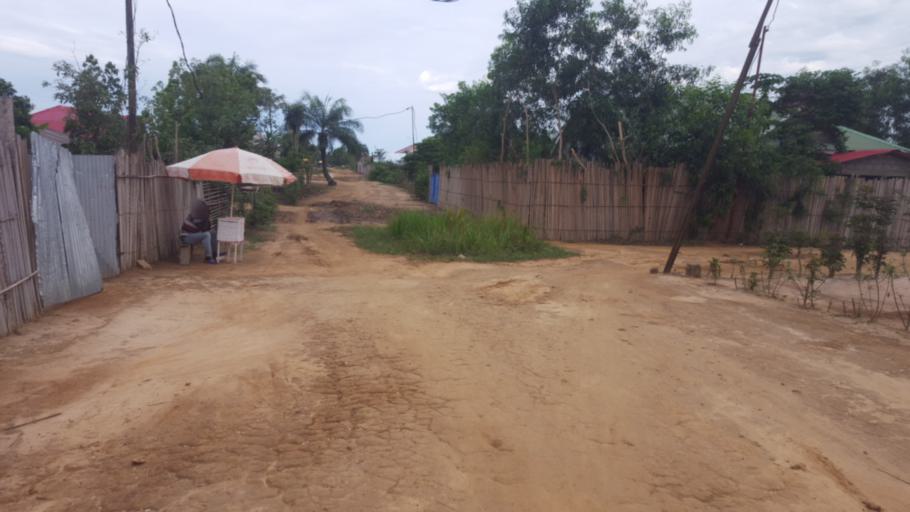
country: CD
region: Bandundu
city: Bandundu
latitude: -3.3025
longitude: 17.3801
